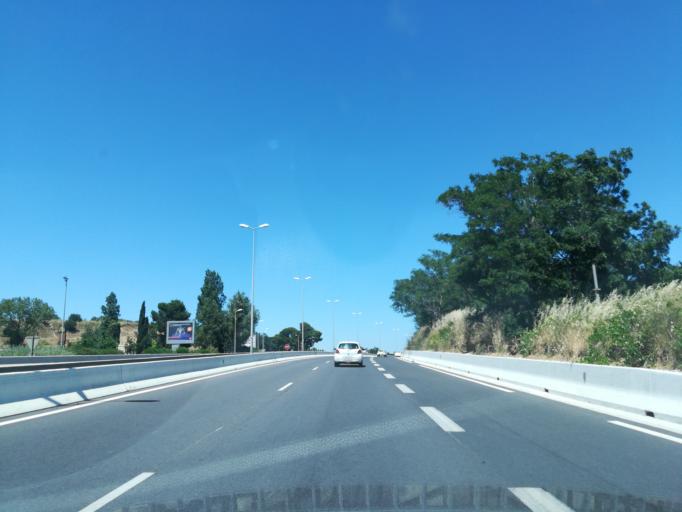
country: FR
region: Languedoc-Roussillon
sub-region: Departement des Pyrenees-Orientales
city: Perpignan
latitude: 42.6695
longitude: 2.8849
